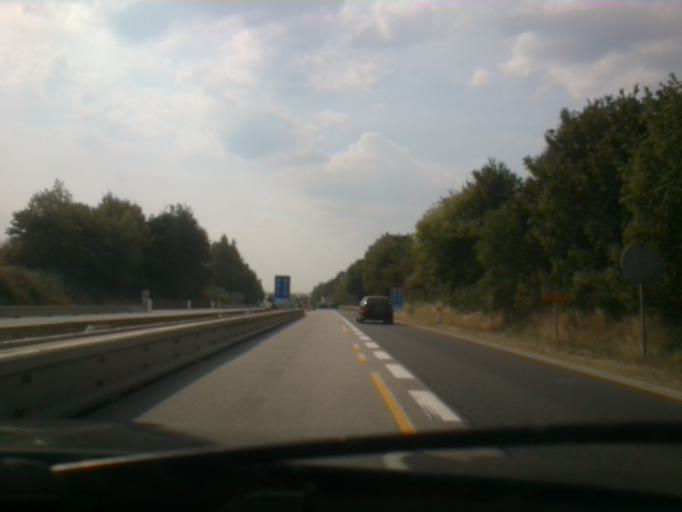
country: CZ
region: Central Bohemia
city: Divisov
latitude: 49.8390
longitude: 14.8286
